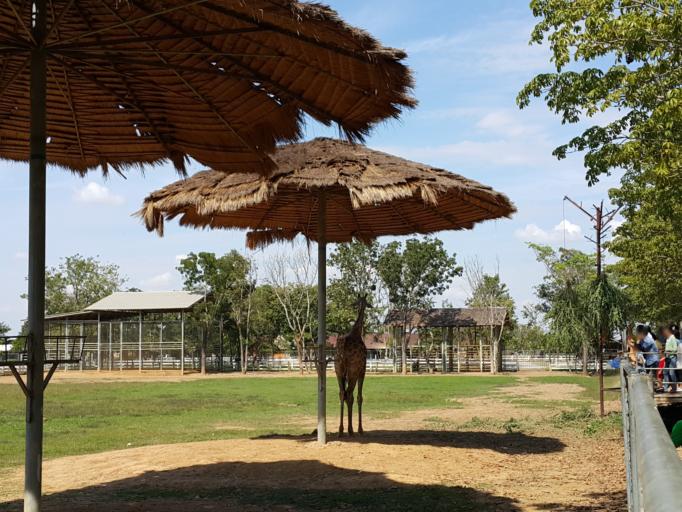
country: TH
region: Sukhothai
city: Si Samrong
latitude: 17.2331
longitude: 99.8208
